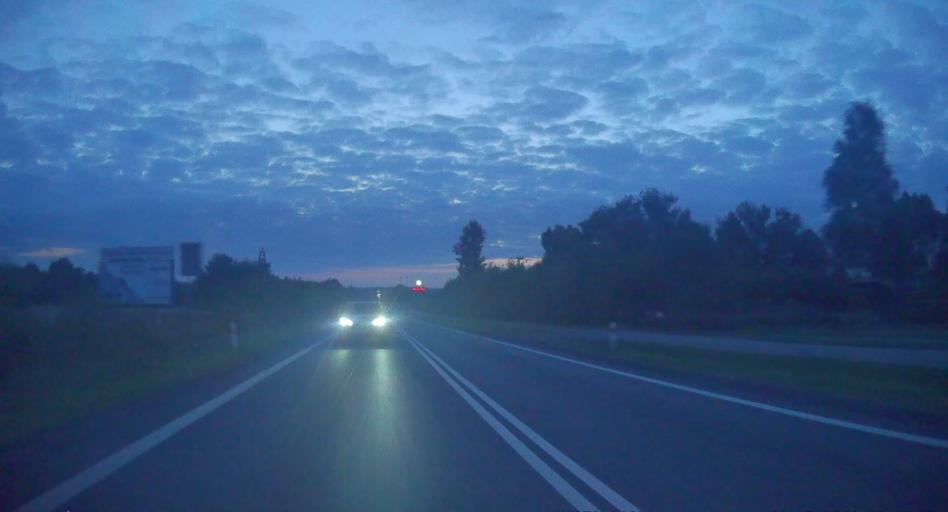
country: PL
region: Silesian Voivodeship
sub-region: Powiat klobucki
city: Klobuck
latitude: 50.8978
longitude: 18.9456
